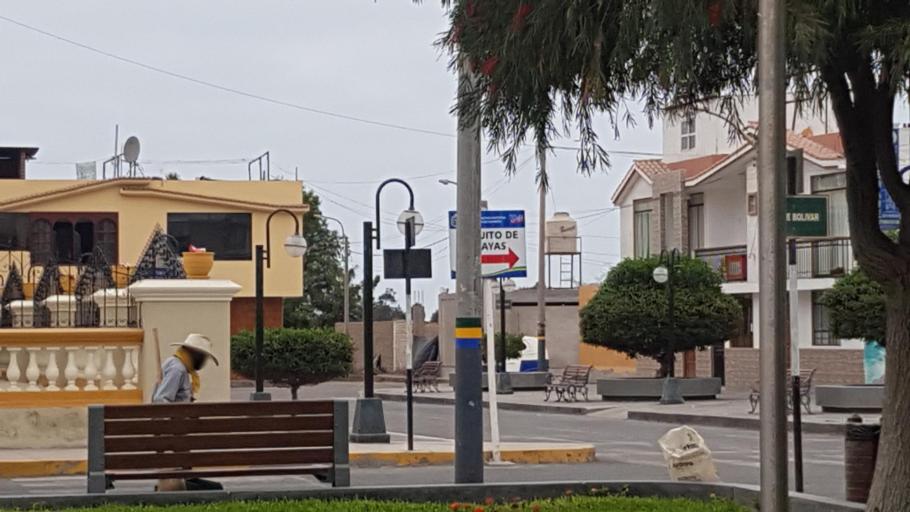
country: PE
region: Arequipa
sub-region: Provincia de Islay
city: Punta de Bombon
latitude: -17.1720
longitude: -71.7903
